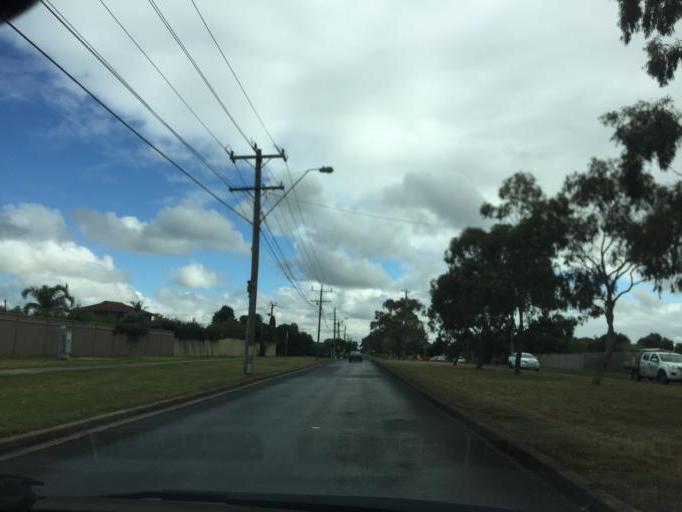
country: AU
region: Victoria
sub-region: Brimbank
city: Sunshine West
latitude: -37.8037
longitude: 144.8189
